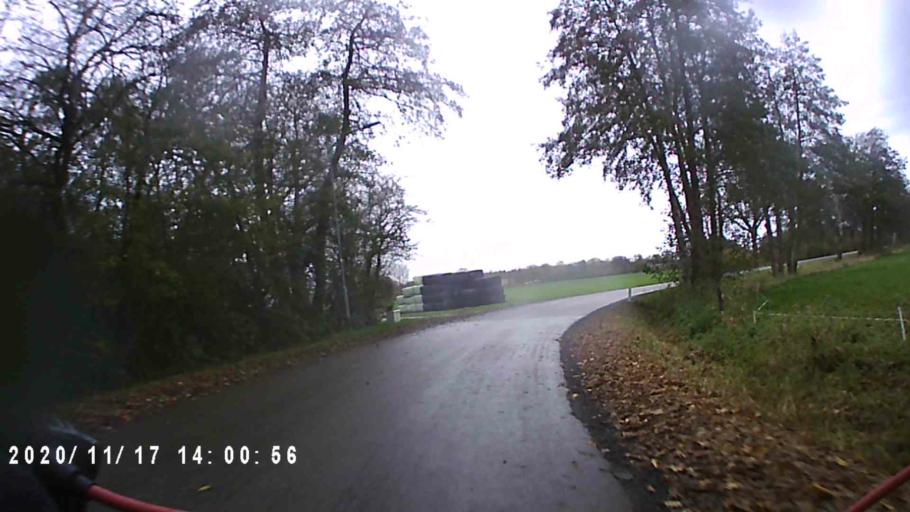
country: NL
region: Groningen
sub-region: Gemeente Zuidhorn
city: Grijpskerk
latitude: 53.2274
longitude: 6.3411
